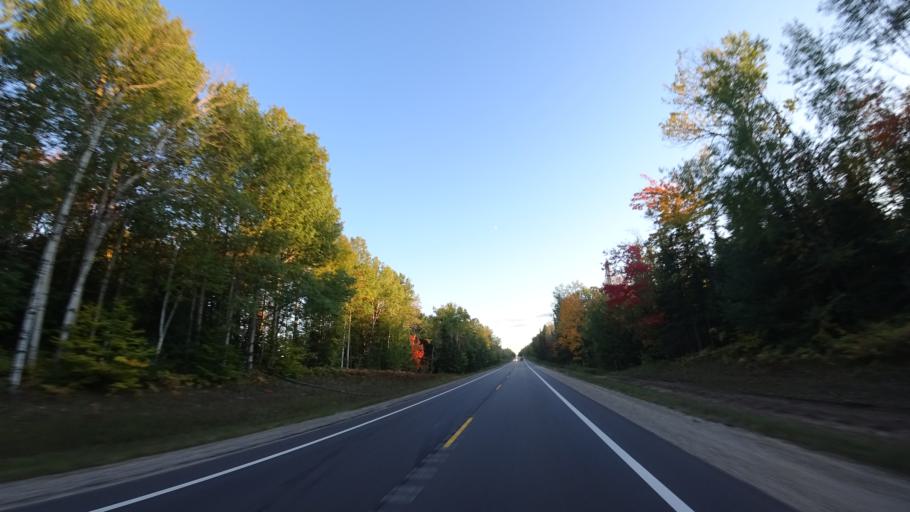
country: US
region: Michigan
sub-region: Luce County
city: Newberry
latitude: 46.2881
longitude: -85.0096
